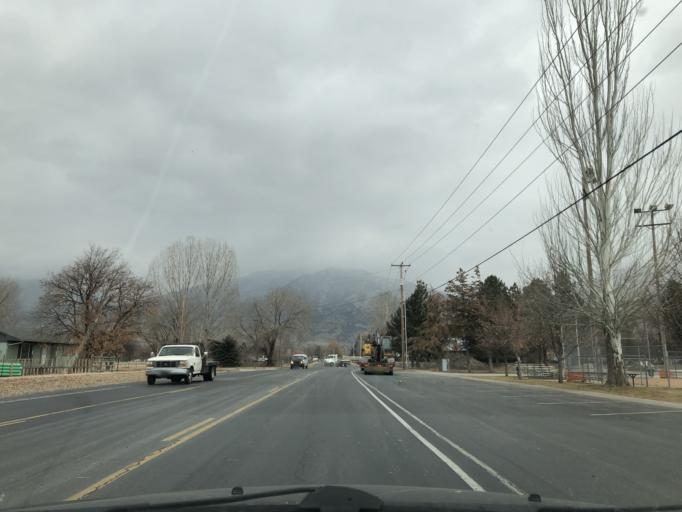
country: US
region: Utah
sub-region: Cache County
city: Nibley
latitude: 41.6749
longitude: -111.8408
